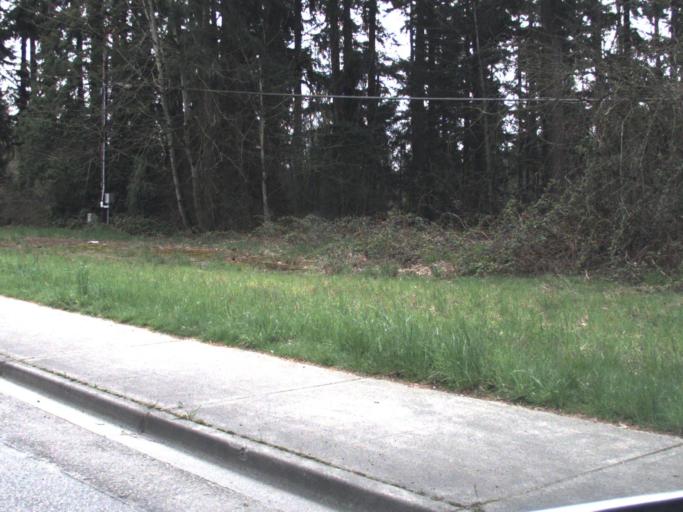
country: US
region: Washington
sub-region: King County
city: Kent
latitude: 47.3769
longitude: -122.2140
